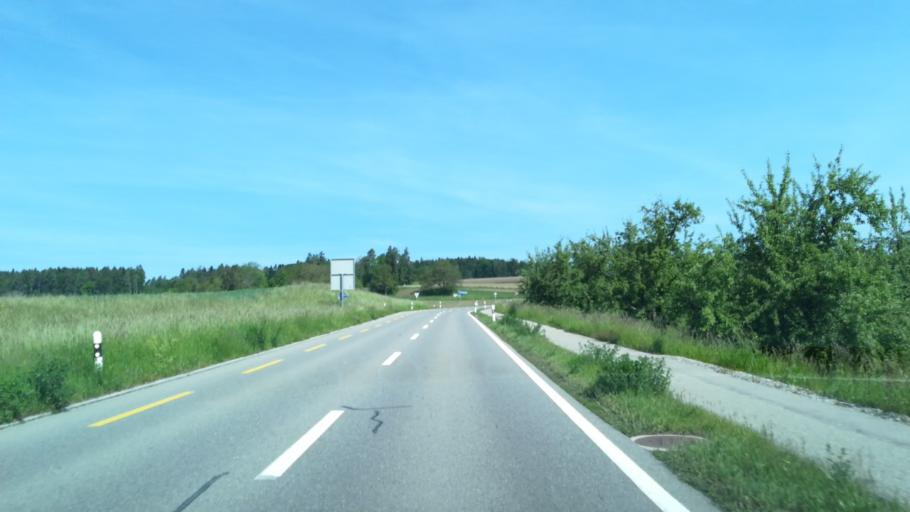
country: CH
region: Thurgau
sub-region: Frauenfeld District
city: Pfyn
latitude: 47.6027
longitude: 8.9466
